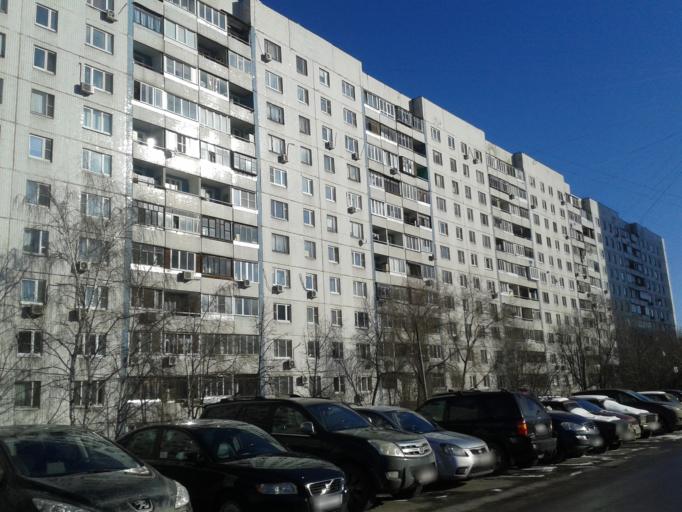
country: RU
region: Moscow
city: Strogino
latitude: 55.8044
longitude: 37.4049
